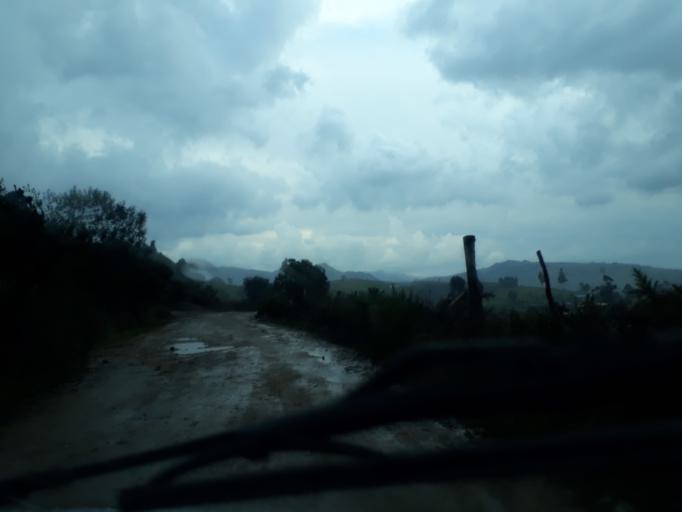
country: CO
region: Cundinamarca
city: Villapinzon
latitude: 5.3029
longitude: -73.5907
